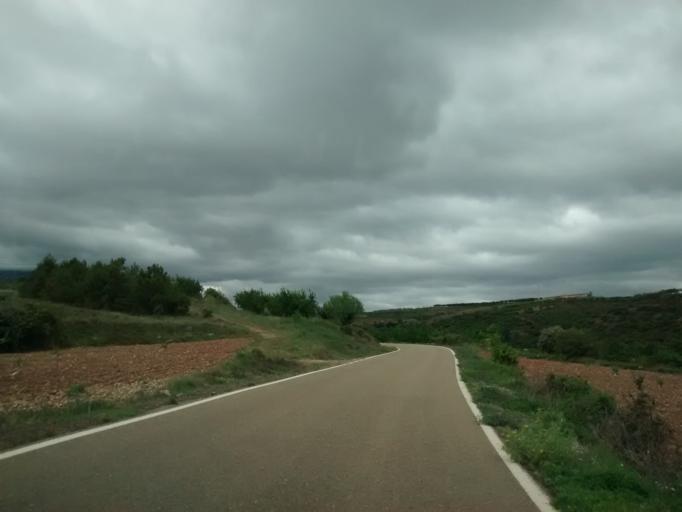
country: ES
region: Aragon
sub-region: Provincia de Zaragoza
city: Lituenigo
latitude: 41.8389
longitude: -1.7480
